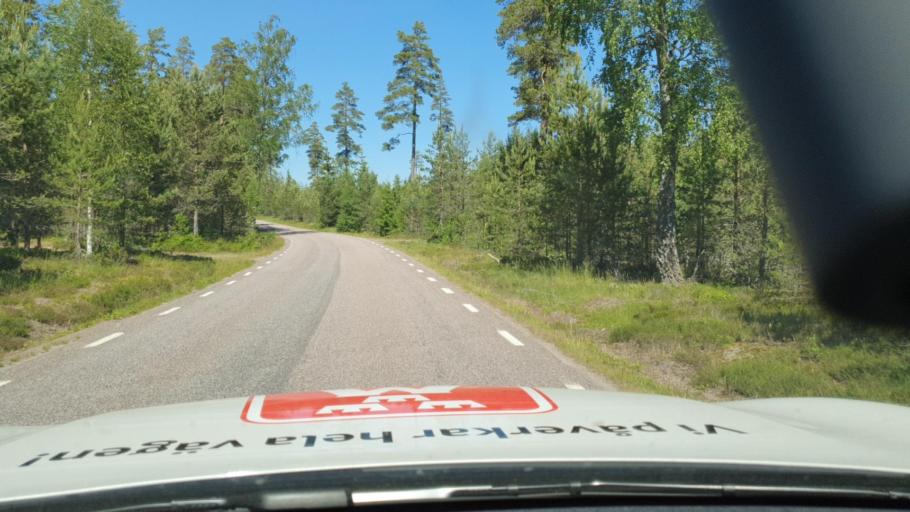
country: SE
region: Joenkoeping
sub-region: Habo Kommun
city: Habo
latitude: 58.0385
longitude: 14.0215
